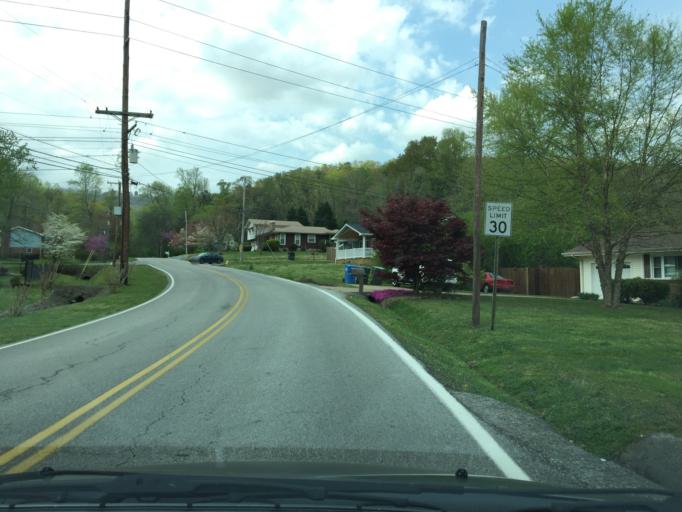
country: US
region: Tennessee
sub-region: Hamilton County
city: Red Bank
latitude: 35.1396
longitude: -85.2847
